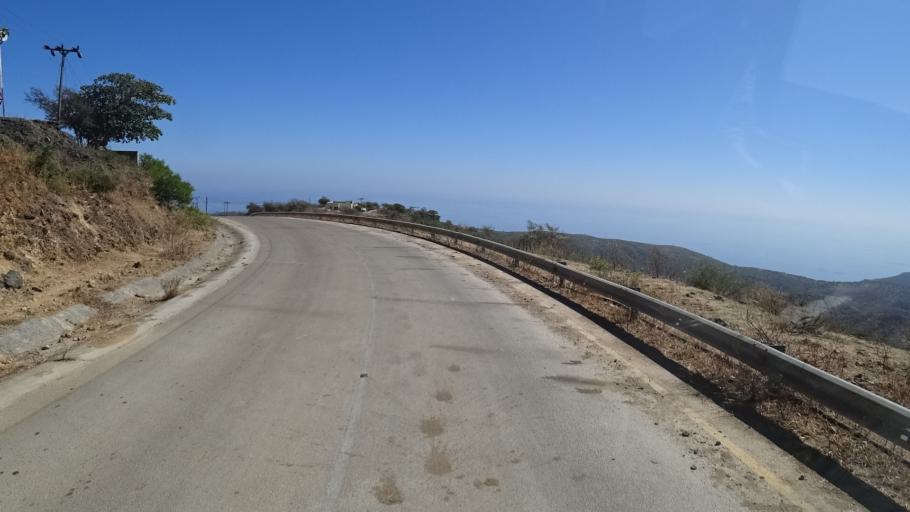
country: YE
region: Al Mahrah
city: Hawf
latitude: 16.7699
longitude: 53.3354
